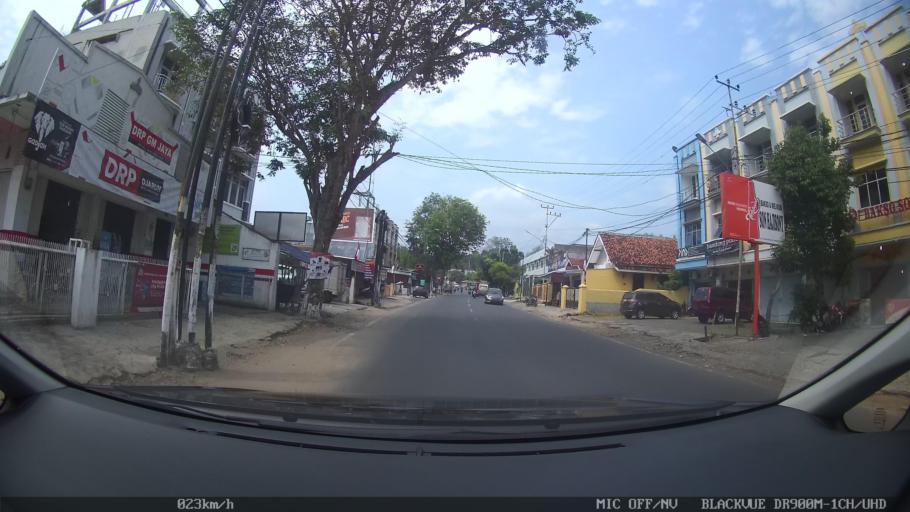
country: ID
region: Lampung
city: Bandarlampung
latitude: -5.4127
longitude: 105.2472
